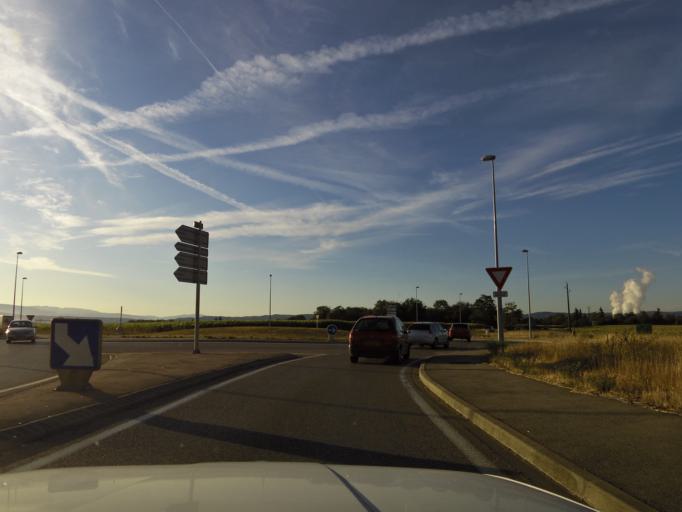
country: FR
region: Rhone-Alpes
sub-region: Departement de l'Ain
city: Chazey-sur-Ain
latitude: 45.8559
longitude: 5.2514
